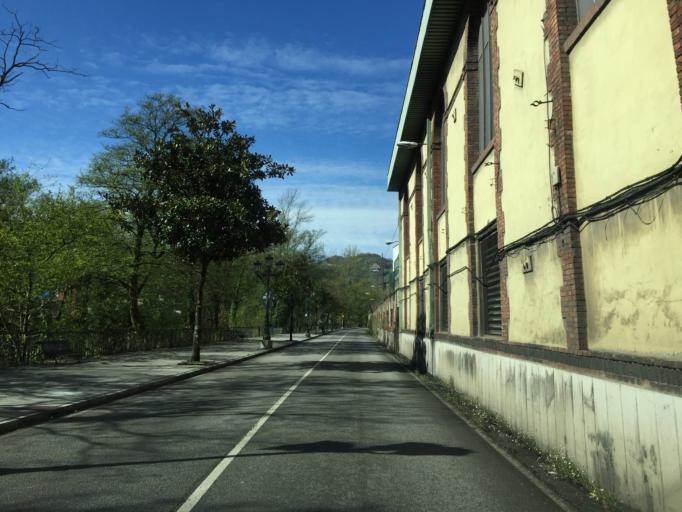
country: ES
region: Asturias
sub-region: Province of Asturias
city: Proaza
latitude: 43.3443
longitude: -5.9742
